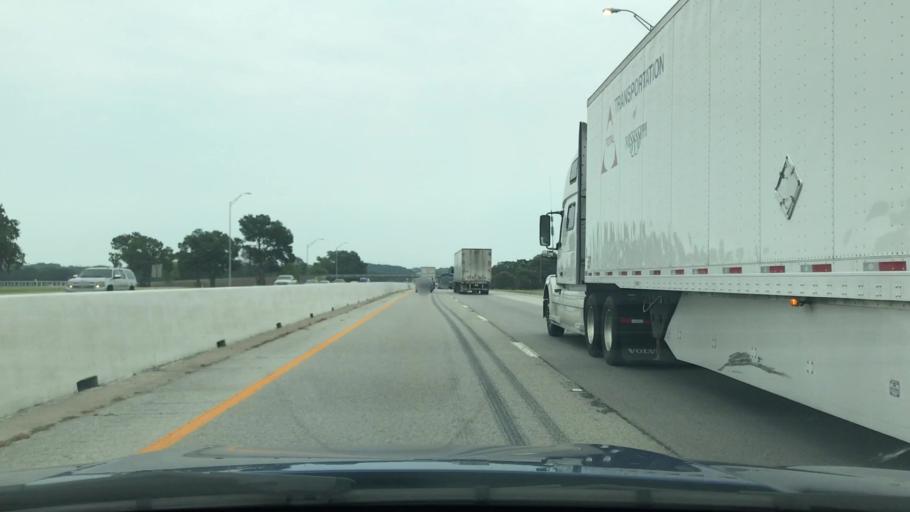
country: US
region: Texas
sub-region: Van Zandt County
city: Van
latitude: 32.4920
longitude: -95.5564
